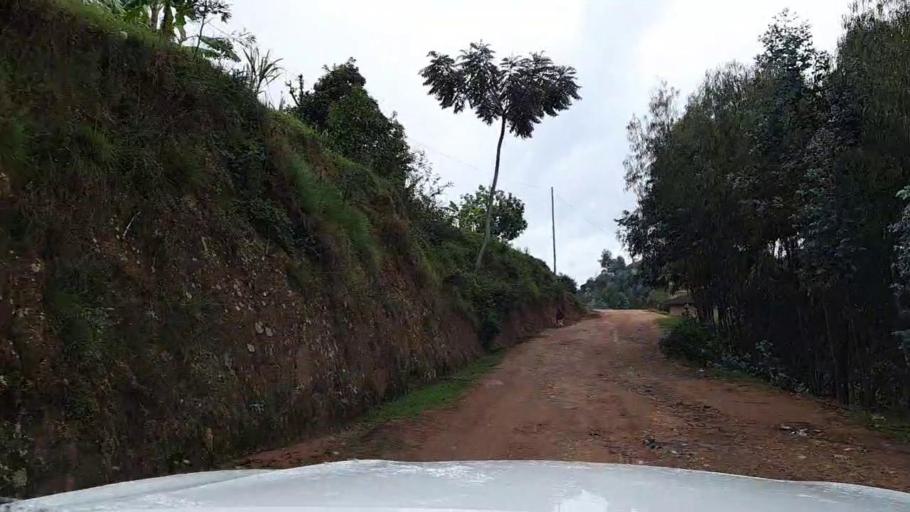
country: RW
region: Southern Province
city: Nzega
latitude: -2.4633
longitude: 29.4940
